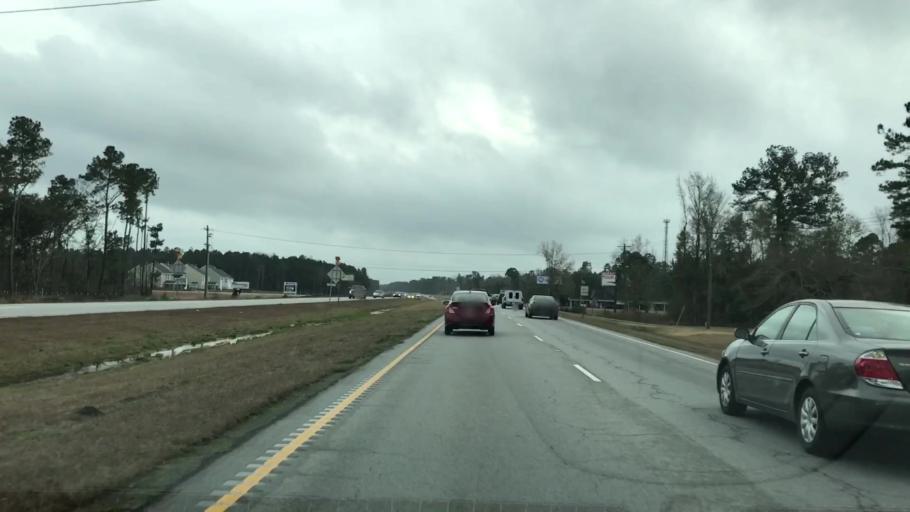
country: US
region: South Carolina
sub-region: Berkeley County
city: Moncks Corner
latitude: 33.1457
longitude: -80.0328
